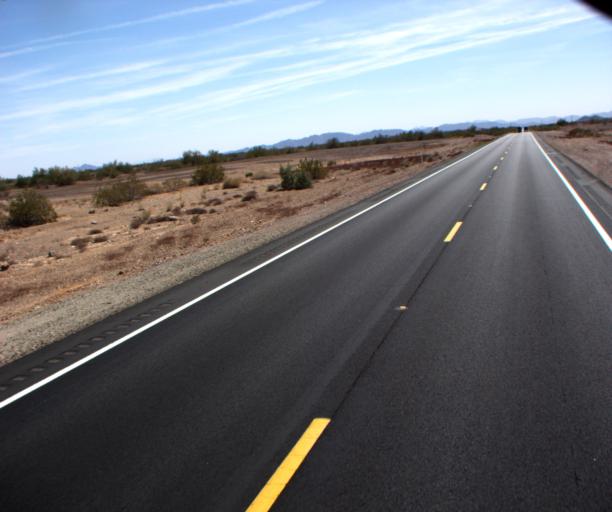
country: US
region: Arizona
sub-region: Yuma County
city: Wellton
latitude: 33.0032
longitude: -114.2855
